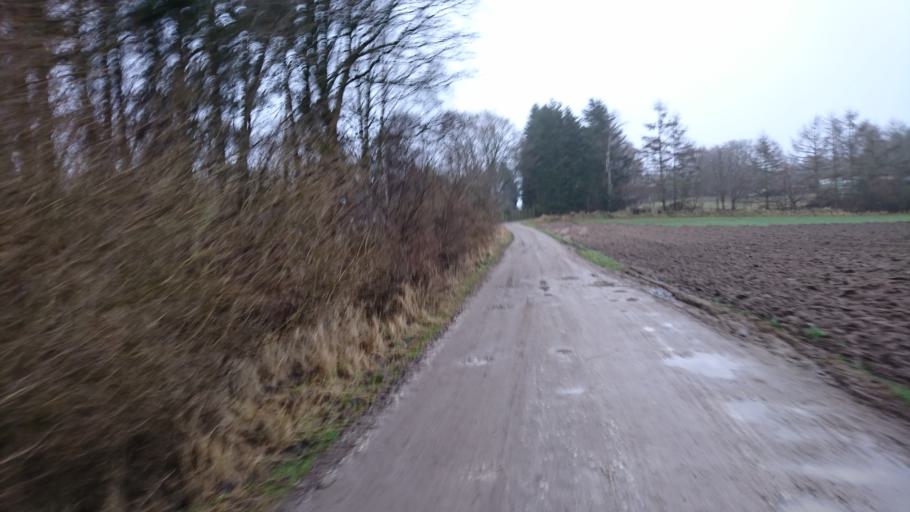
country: DK
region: Capital Region
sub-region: Ballerup Kommune
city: Ballerup
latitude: 55.7446
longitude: 12.3464
